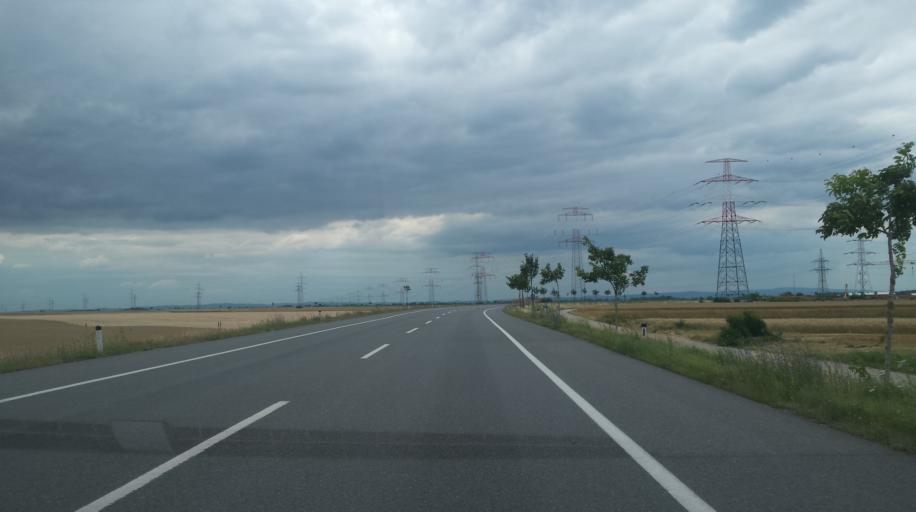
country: AT
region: Lower Austria
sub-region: Politischer Bezirk Wien-Umgebung
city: Himberg
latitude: 48.0801
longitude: 16.4603
